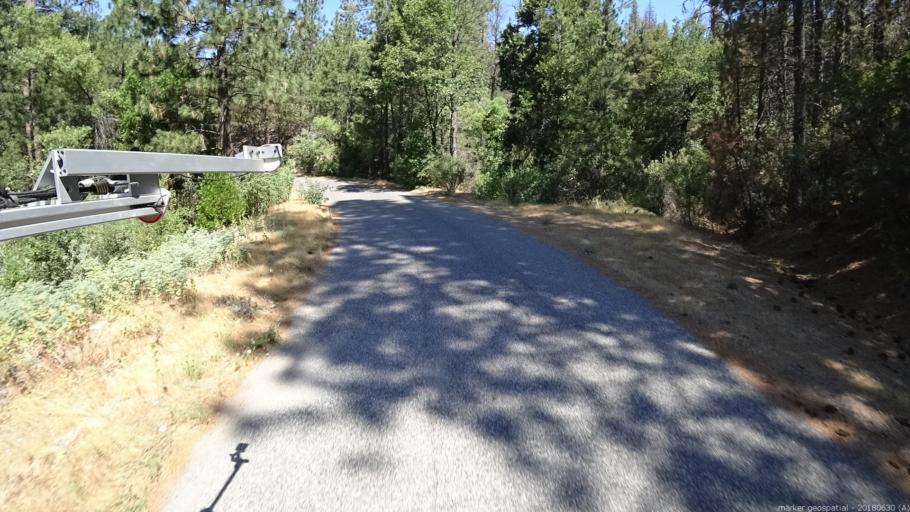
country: US
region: California
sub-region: Madera County
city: Oakhurst
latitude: 37.3592
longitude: -119.3448
